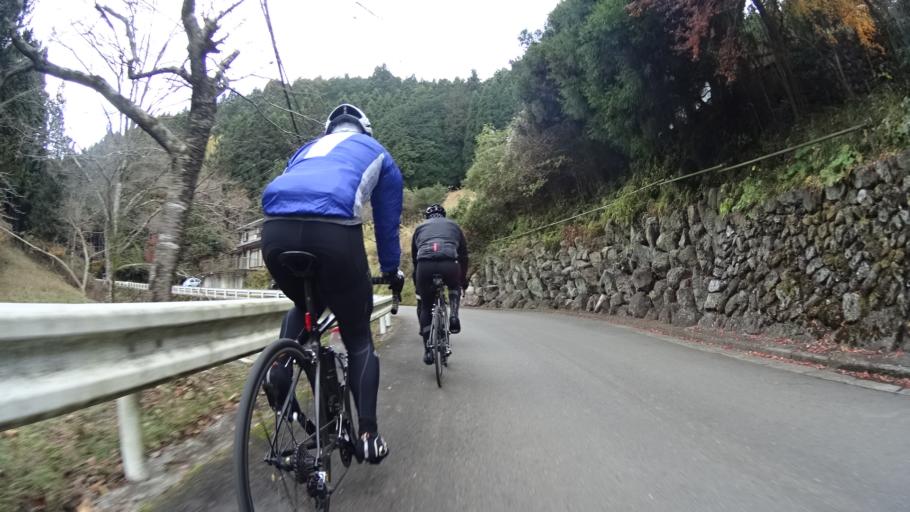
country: JP
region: Saitama
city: Morohongo
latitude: 35.9212
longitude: 139.1882
